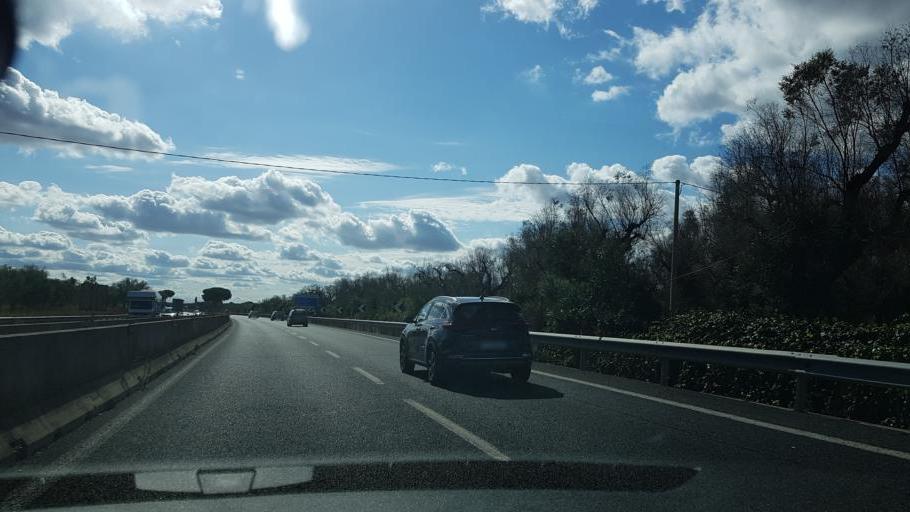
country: IT
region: Apulia
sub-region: Provincia di Brindisi
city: Torchiarolo
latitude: 40.4690
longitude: 18.0520
